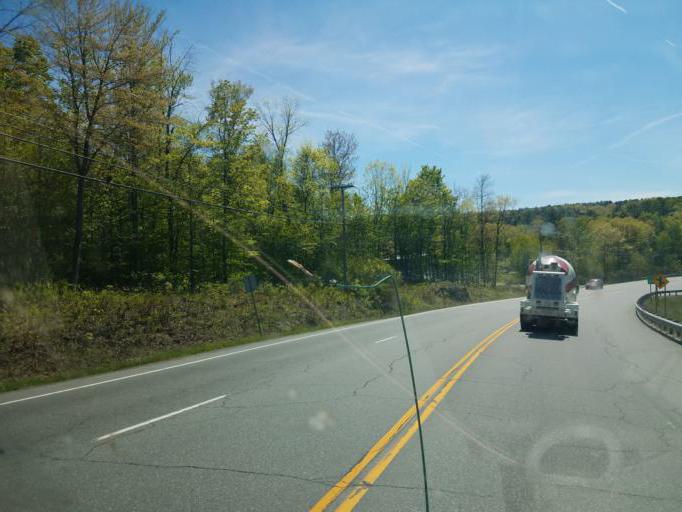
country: US
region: New Hampshire
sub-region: Grafton County
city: Lebanon
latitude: 43.6349
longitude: -72.2057
